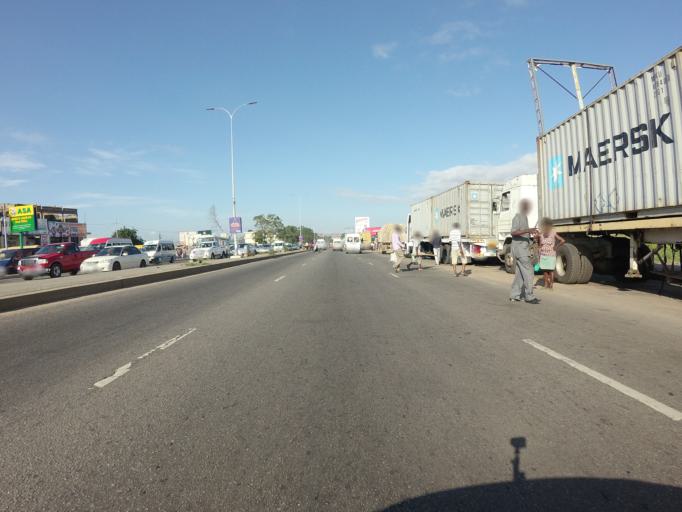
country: GH
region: Greater Accra
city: Gbawe
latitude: 5.5793
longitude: -0.2669
